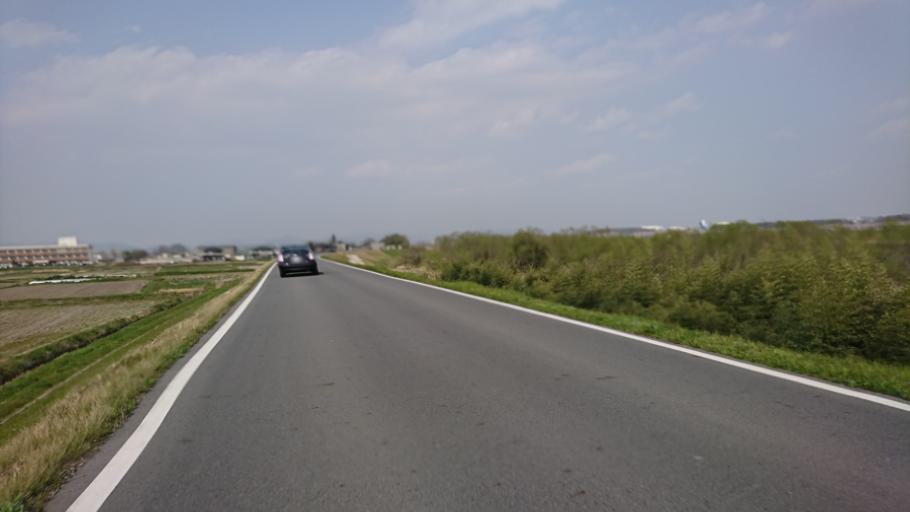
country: JP
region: Hyogo
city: Ono
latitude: 34.8662
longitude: 134.9177
